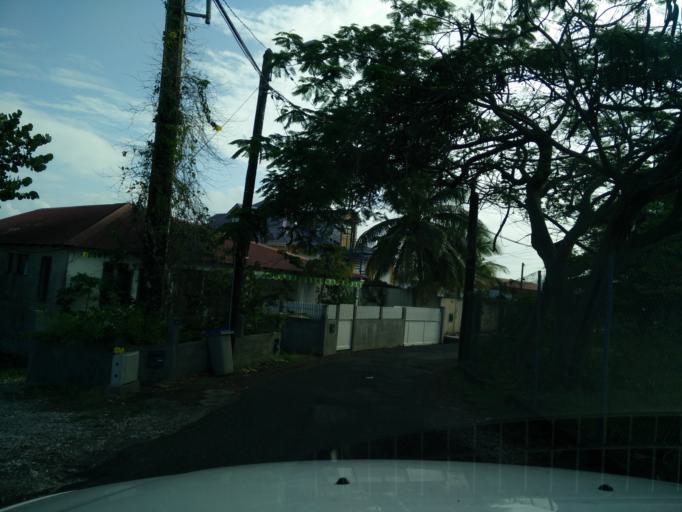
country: GP
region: Guadeloupe
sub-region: Guadeloupe
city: Sainte-Anne
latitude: 16.2259
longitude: -61.3867
